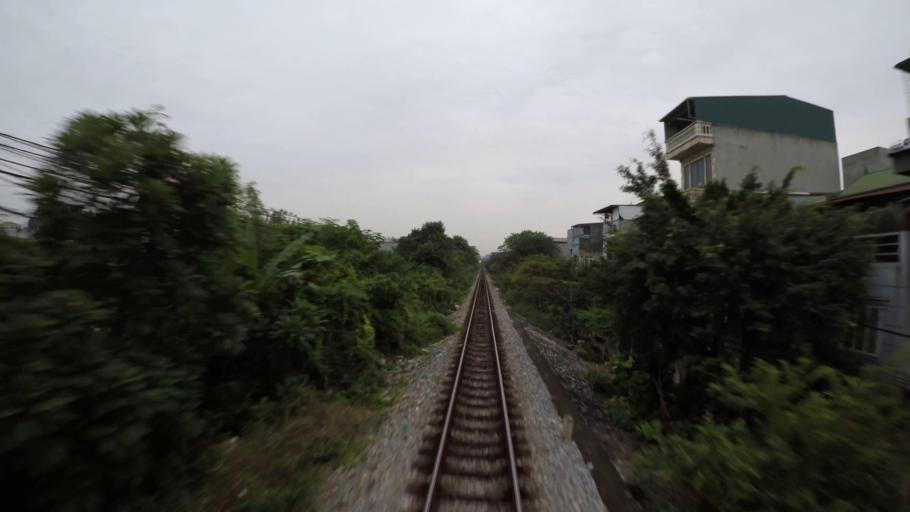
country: VN
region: Ha Noi
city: Hoan Kiem
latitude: 21.0435
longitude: 105.8958
